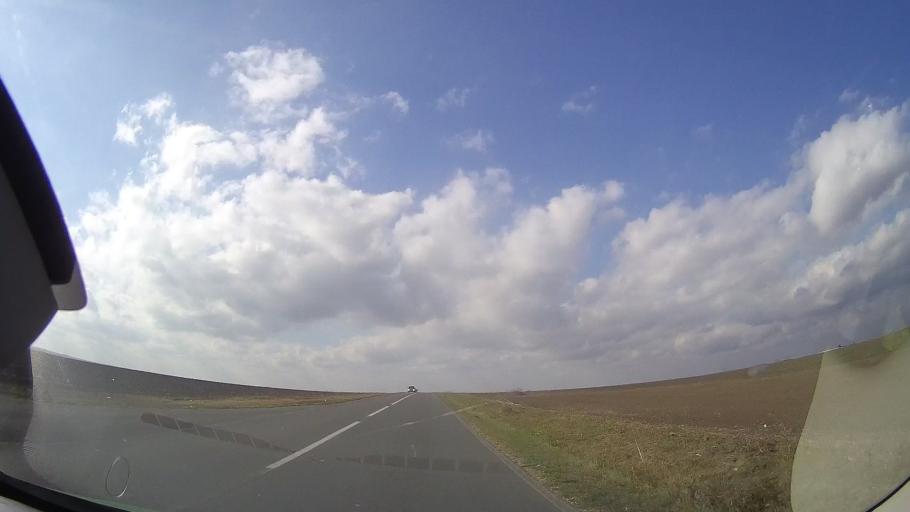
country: RO
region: Constanta
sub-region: Comuna Douazeci si Trei August
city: Douazeci si Trei August
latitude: 43.9138
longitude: 28.5746
